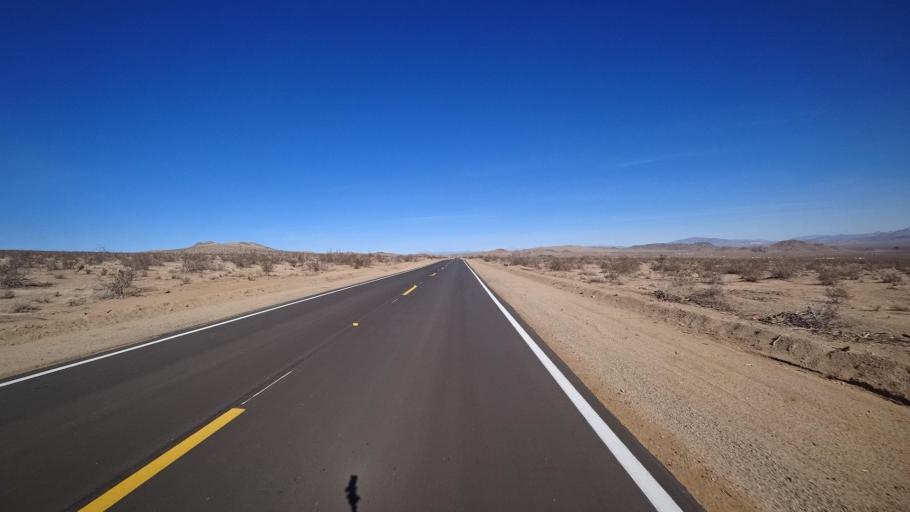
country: US
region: California
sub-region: Kern County
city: Ridgecrest
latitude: 35.5246
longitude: -117.5991
